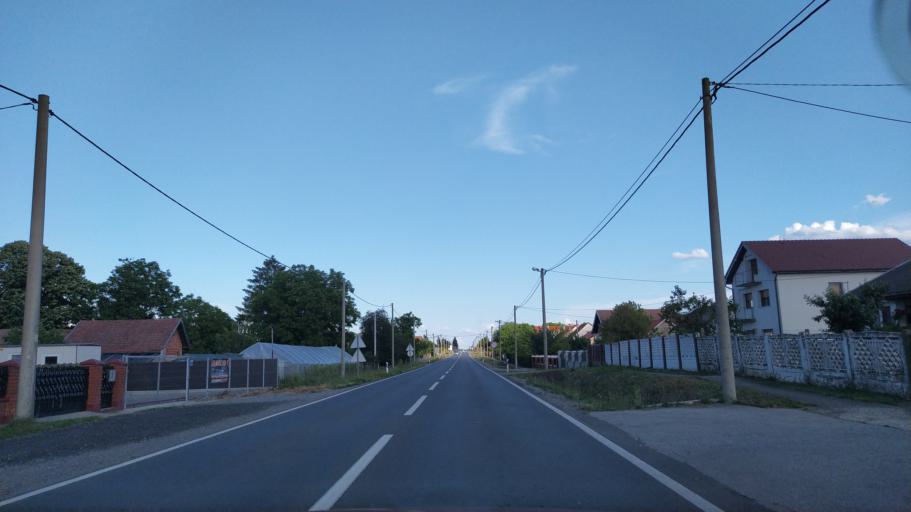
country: HR
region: Virovitick-Podravska
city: Spisic-Bukovica
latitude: 45.8510
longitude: 17.3322
